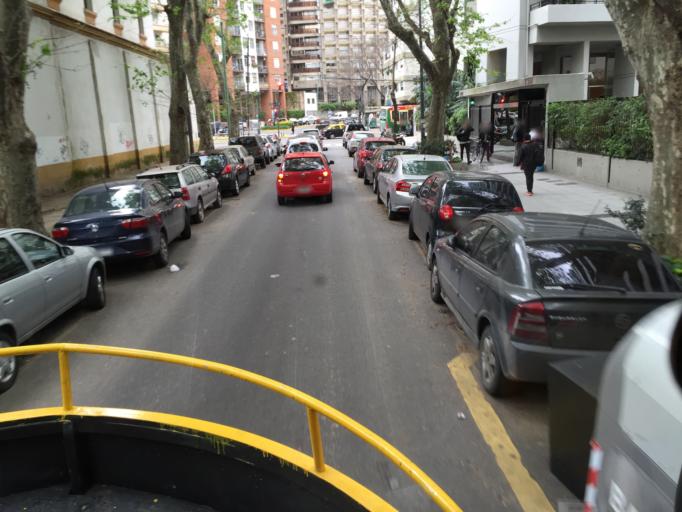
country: AR
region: Buenos Aires F.D.
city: Colegiales
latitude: -34.5738
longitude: -58.4313
